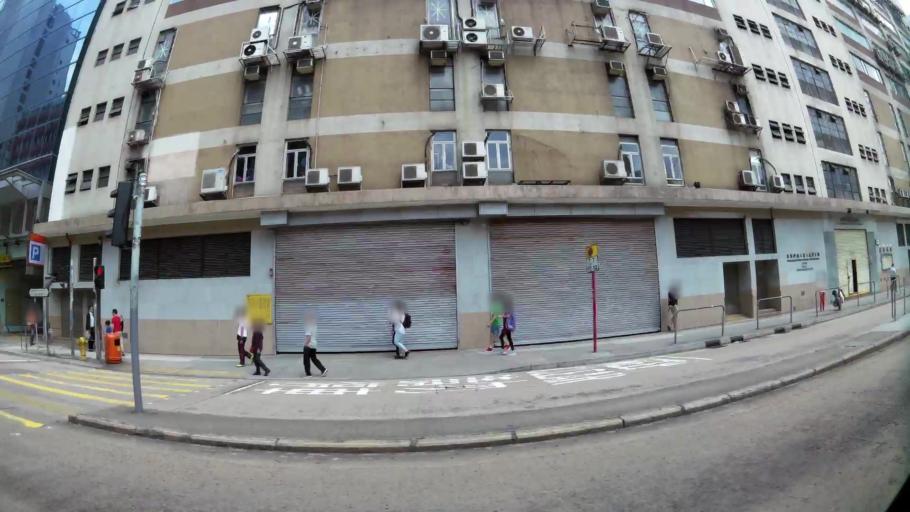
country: HK
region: Sham Shui Po
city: Sham Shui Po
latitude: 22.3381
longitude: 114.1508
